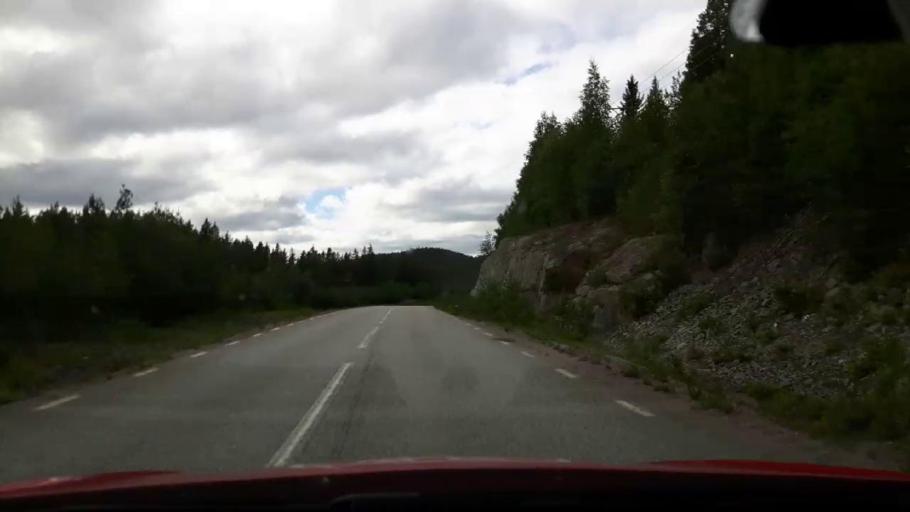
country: SE
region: Jaemtland
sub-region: Ragunda Kommun
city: Hammarstrand
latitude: 62.9641
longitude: 16.0263
